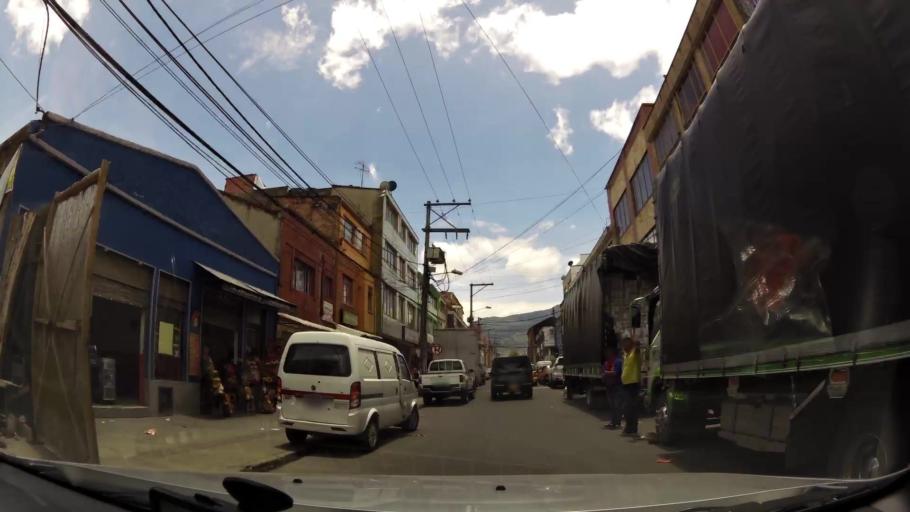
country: CO
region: Bogota D.C.
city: Bogota
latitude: 4.5858
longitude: -74.0989
